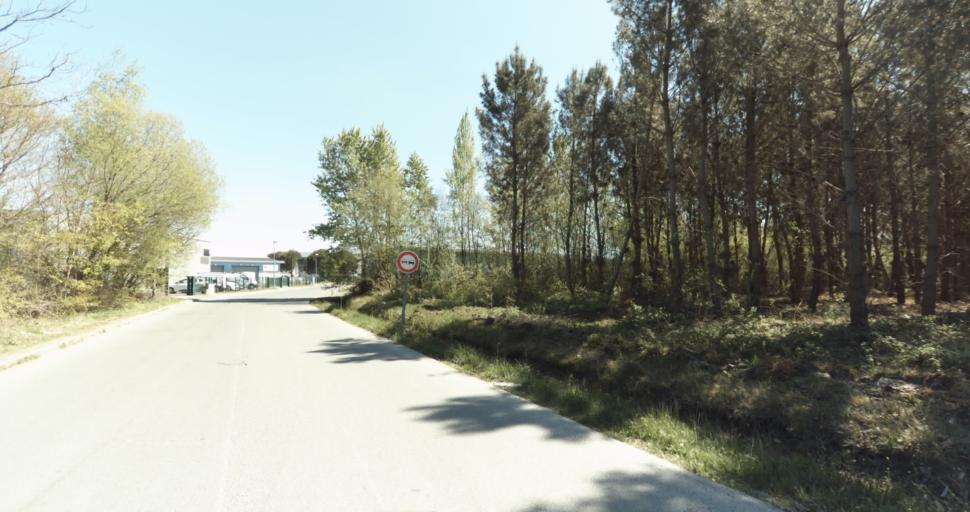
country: FR
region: Aquitaine
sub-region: Departement de la Gironde
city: Martignas-sur-Jalle
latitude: 44.8094
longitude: -0.7519
